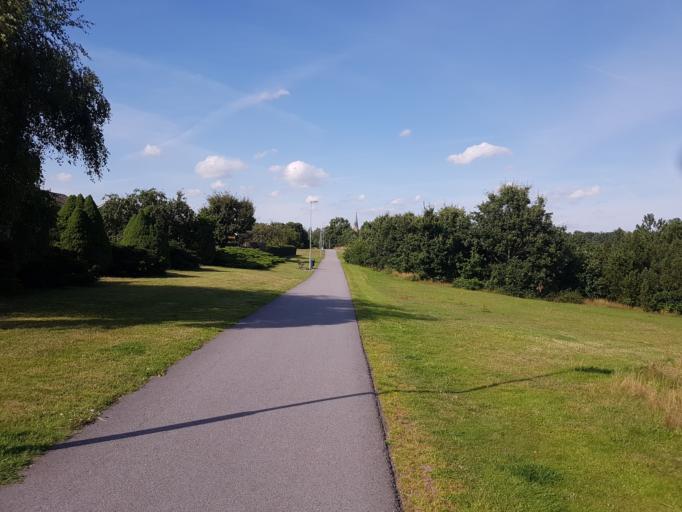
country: SE
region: Skane
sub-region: Sjobo Kommun
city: Sjoebo
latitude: 55.6395
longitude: 13.6999
